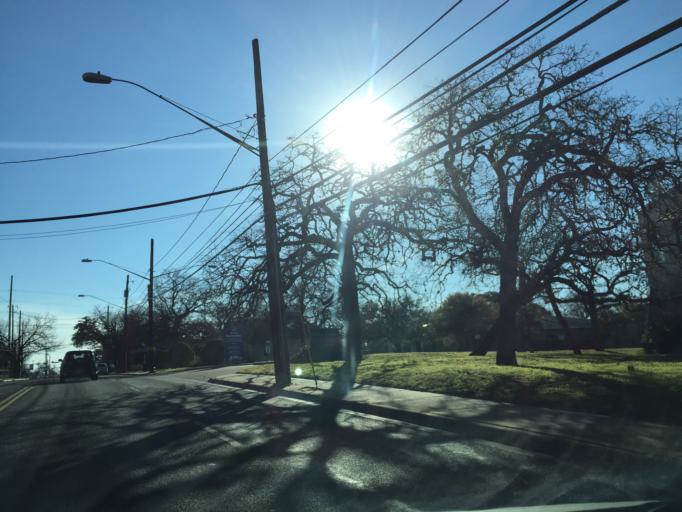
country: US
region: Texas
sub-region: Travis County
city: Austin
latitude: 30.2291
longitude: -97.7679
